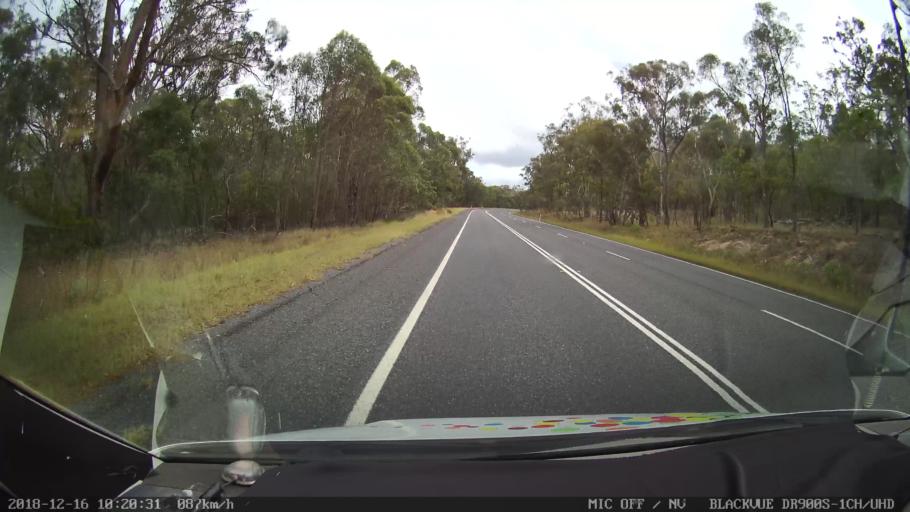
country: AU
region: New South Wales
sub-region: Tenterfield Municipality
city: Carrolls Creek
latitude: -29.2190
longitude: 152.0097
